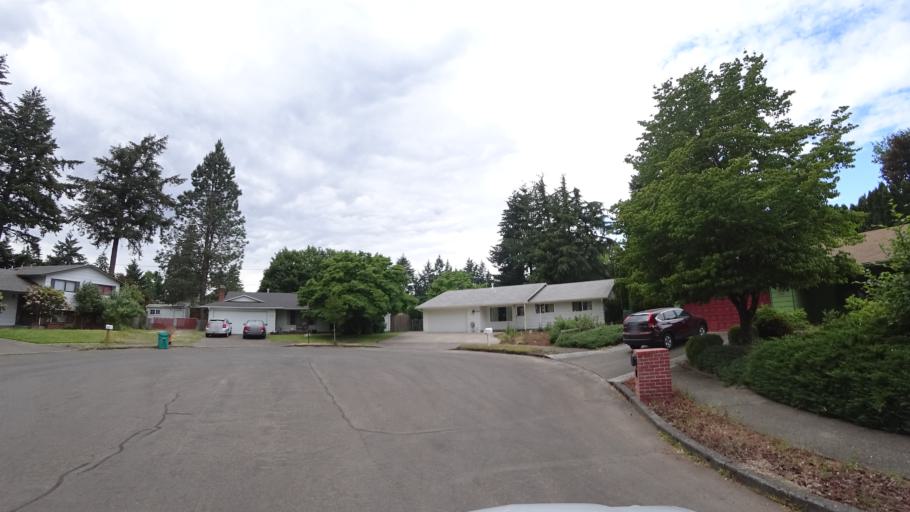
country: US
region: Oregon
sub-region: Clackamas County
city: Happy Valley
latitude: 45.5023
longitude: -122.5035
